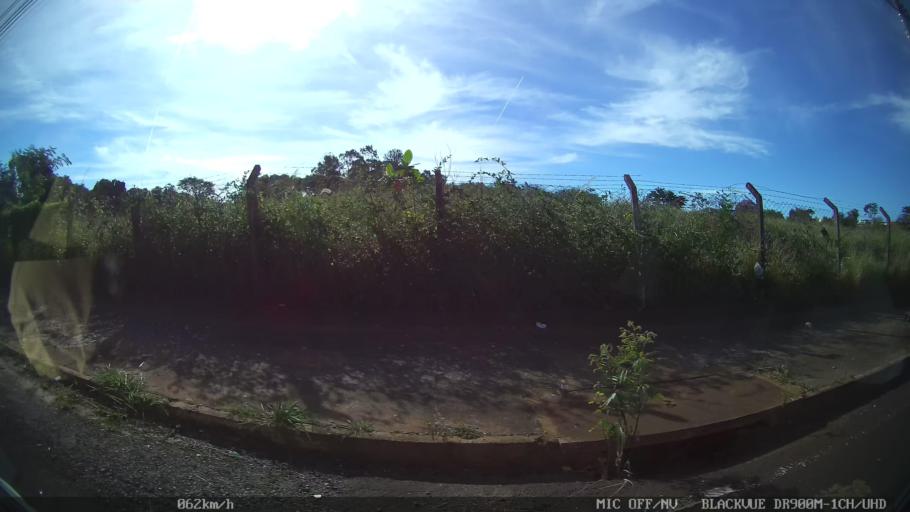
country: BR
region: Sao Paulo
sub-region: Sao Jose Do Rio Preto
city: Sao Jose do Rio Preto
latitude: -20.8017
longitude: -49.3513
